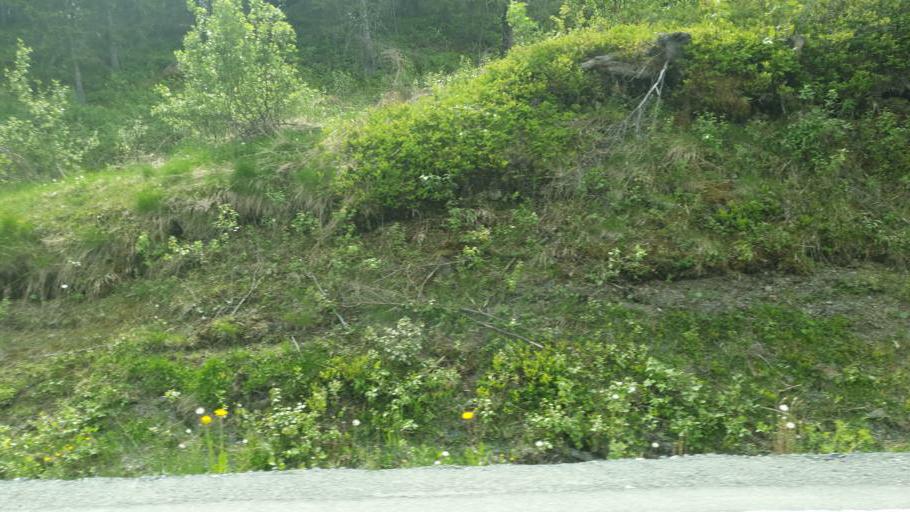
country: NO
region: Nord-Trondelag
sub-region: Leksvik
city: Leksvik
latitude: 63.6894
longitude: 10.5269
